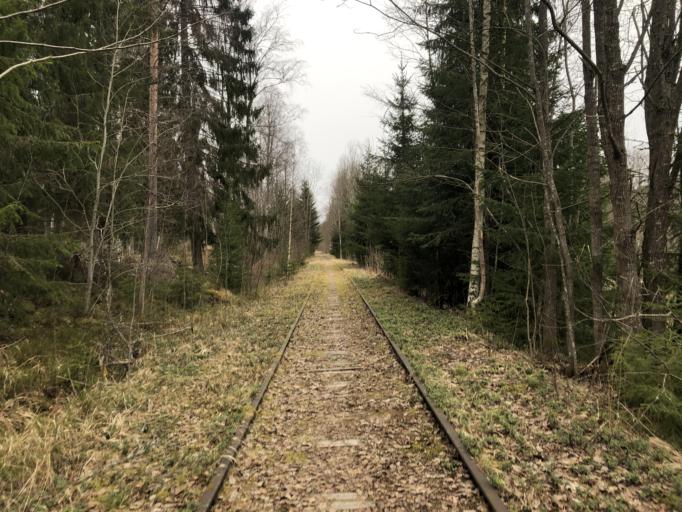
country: SE
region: Vaermland
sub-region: Filipstads Kommun
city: Lesjofors
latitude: 59.9695
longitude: 14.1904
